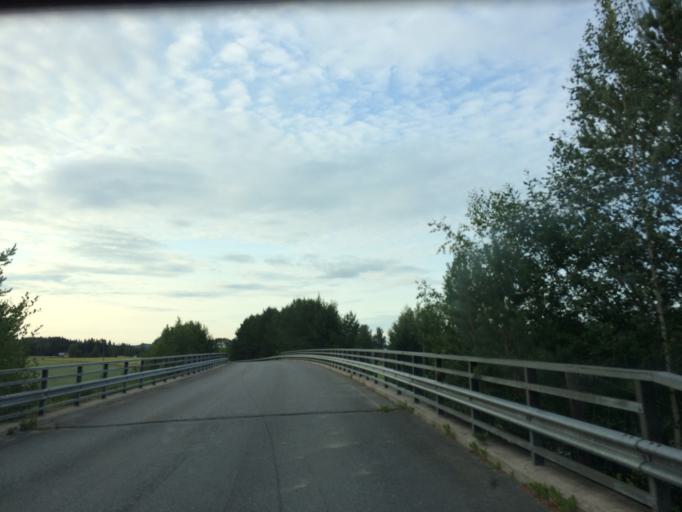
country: FI
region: Haeme
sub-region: Haemeenlinna
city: Tervakoski
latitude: 60.8436
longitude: 24.6273
